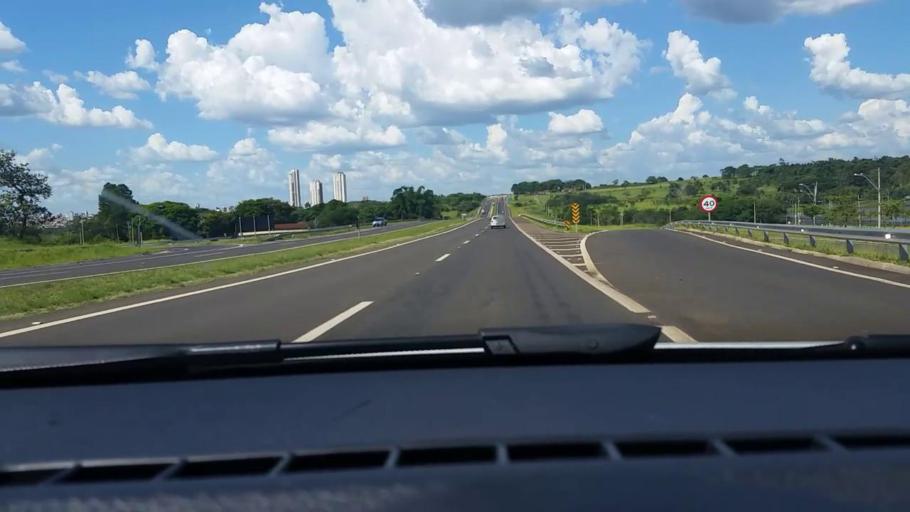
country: BR
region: Sao Paulo
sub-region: Bauru
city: Bauru
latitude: -22.3874
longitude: -49.0735
